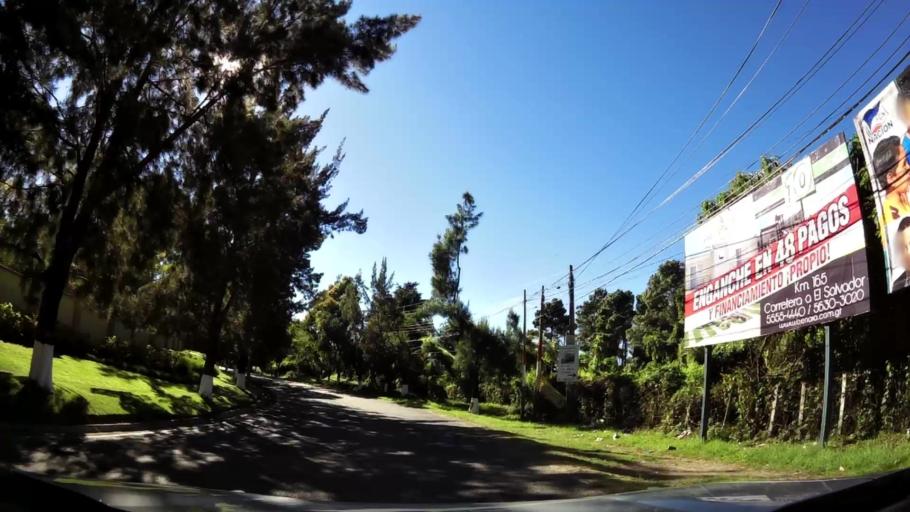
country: GT
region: Guatemala
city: Fraijanes
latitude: 14.5070
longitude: -90.4656
